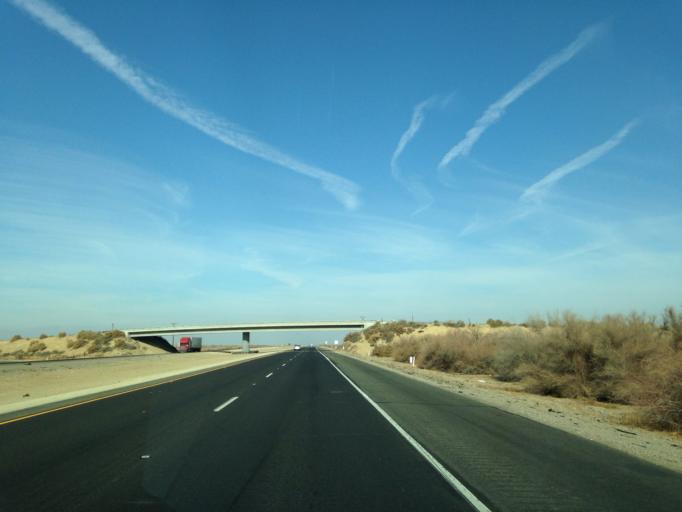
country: US
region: California
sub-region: Kern County
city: Lost Hills
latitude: 35.7883
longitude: -119.7810
